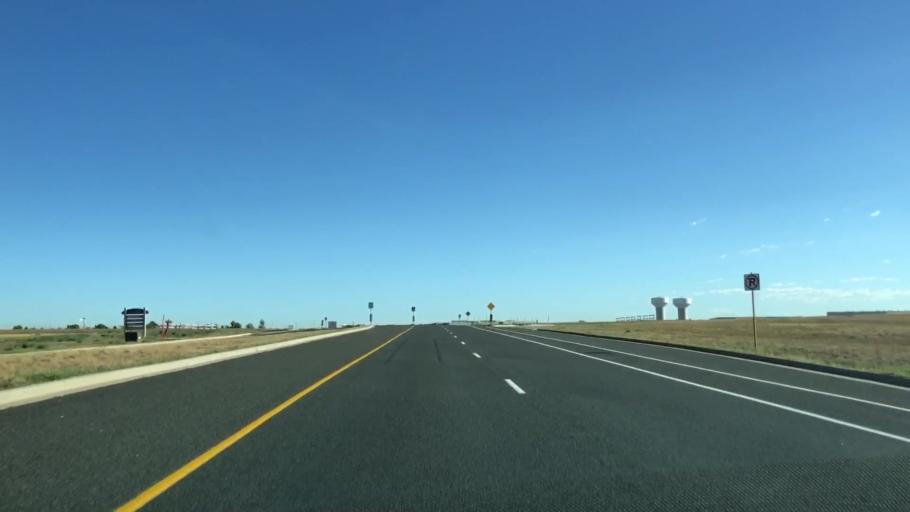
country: US
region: Colorado
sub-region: Larimer County
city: Loveland
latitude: 40.4244
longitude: -104.9840
